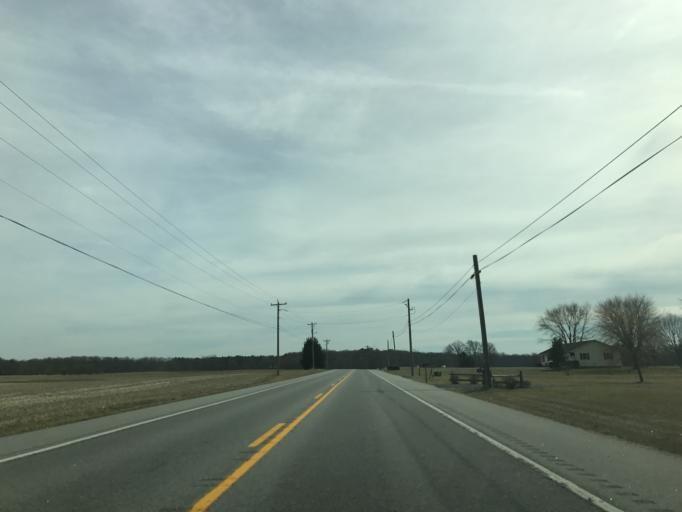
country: US
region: Maryland
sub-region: Queen Anne's County
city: Centreville
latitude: 39.0910
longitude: -76.0338
